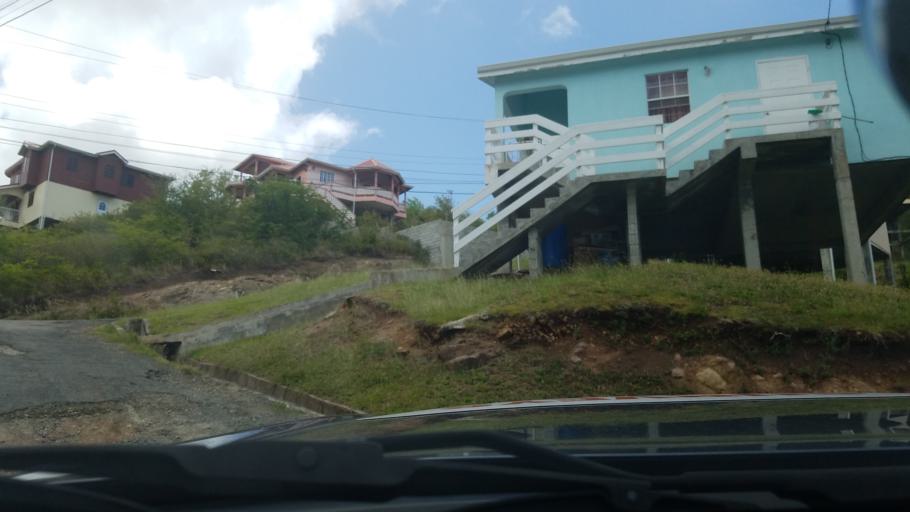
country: LC
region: Gros-Islet
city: Gros Islet
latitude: 14.0571
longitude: -60.9311
